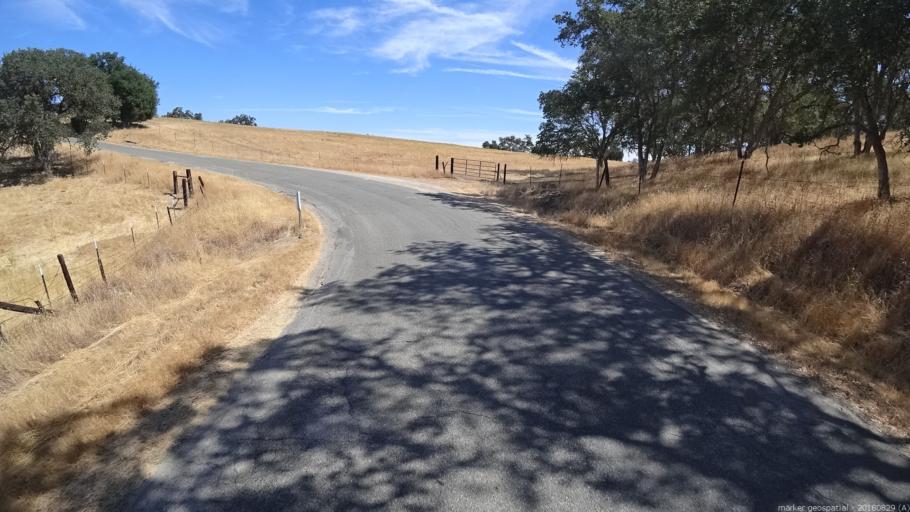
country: US
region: California
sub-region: San Luis Obispo County
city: Lake Nacimiento
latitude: 35.8086
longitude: -121.0569
